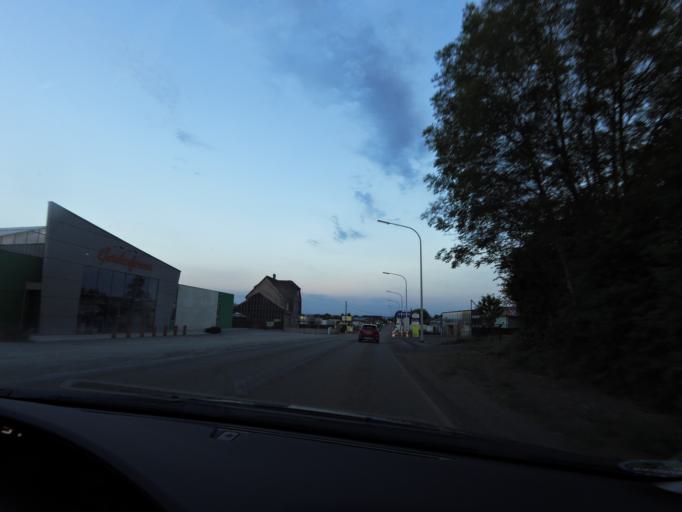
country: BE
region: Wallonia
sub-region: Province de Liege
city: Welkenraedt
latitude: 50.6752
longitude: 5.9678
